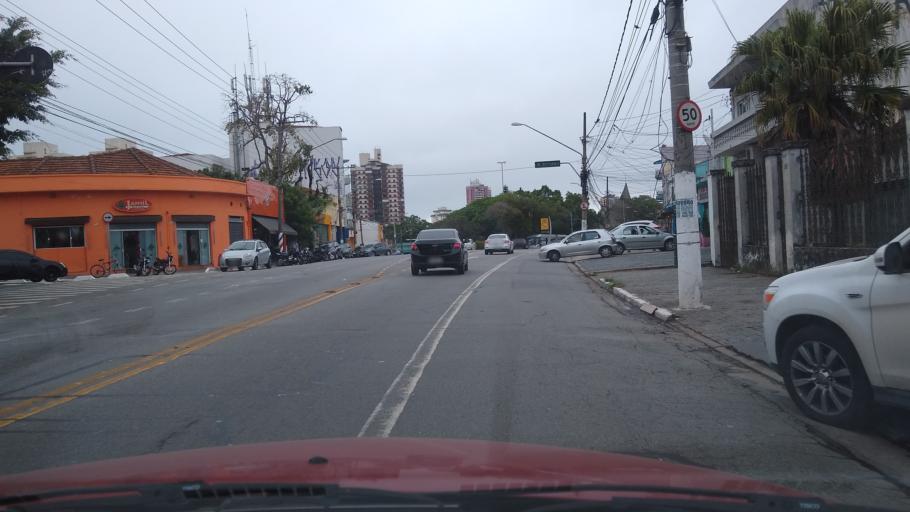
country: BR
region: Sao Paulo
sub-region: Sao Caetano Do Sul
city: Sao Caetano do Sul
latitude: -23.6170
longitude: -46.6180
